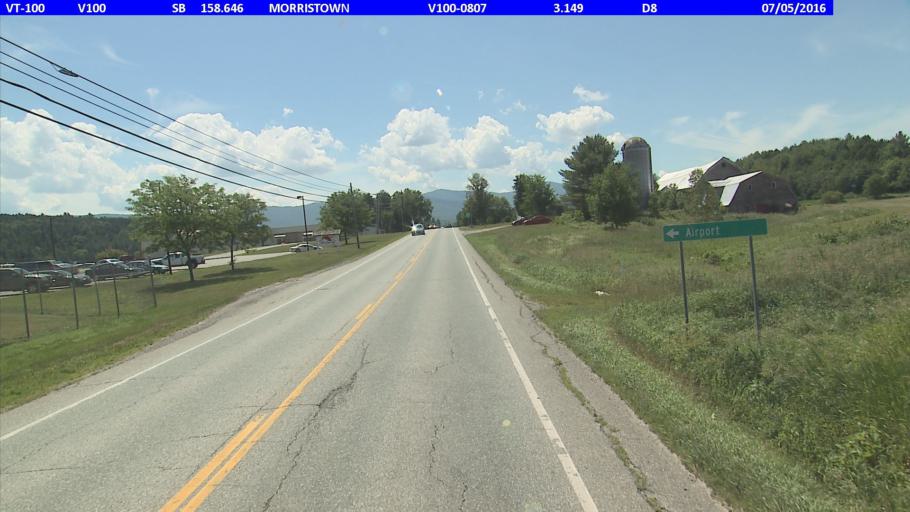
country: US
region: Vermont
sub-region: Lamoille County
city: Morristown
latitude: 44.5374
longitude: -72.6169
